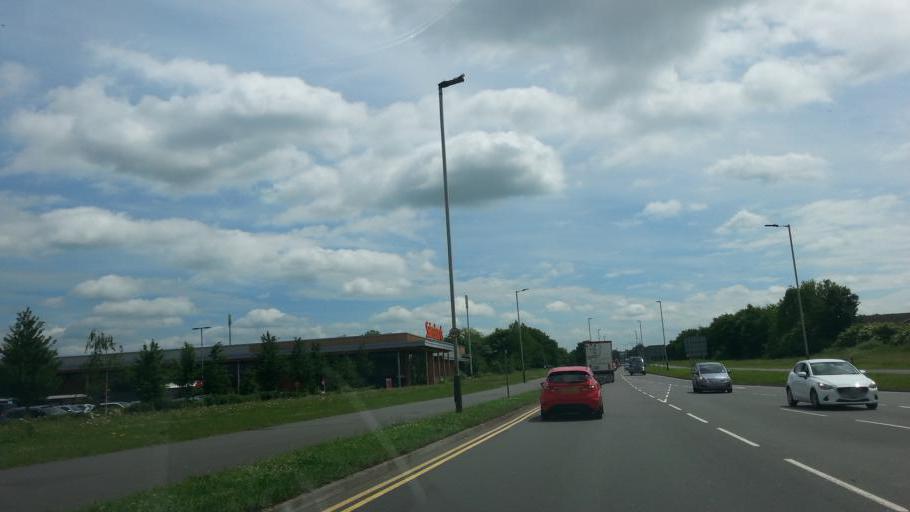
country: GB
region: England
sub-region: City of Leicester
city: Leicester
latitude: 52.6673
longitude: -1.1066
